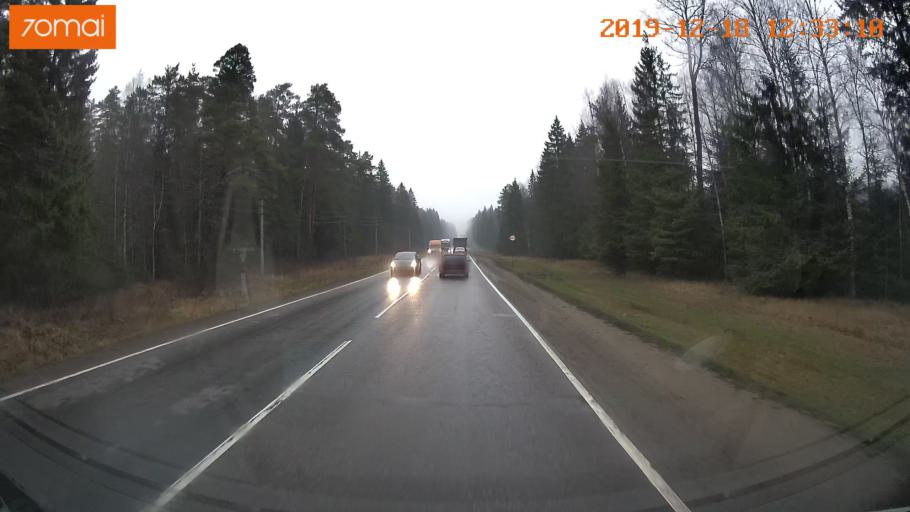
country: RU
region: Moskovskaya
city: Rumyantsevo
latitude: 56.1108
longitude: 36.5582
